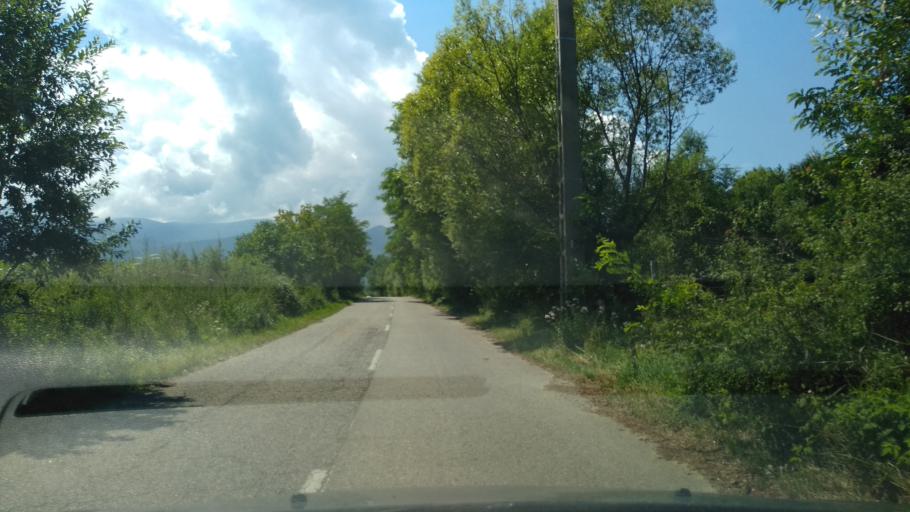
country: RO
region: Hunedoara
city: Salasu de Sus
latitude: 45.5049
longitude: 22.9505
